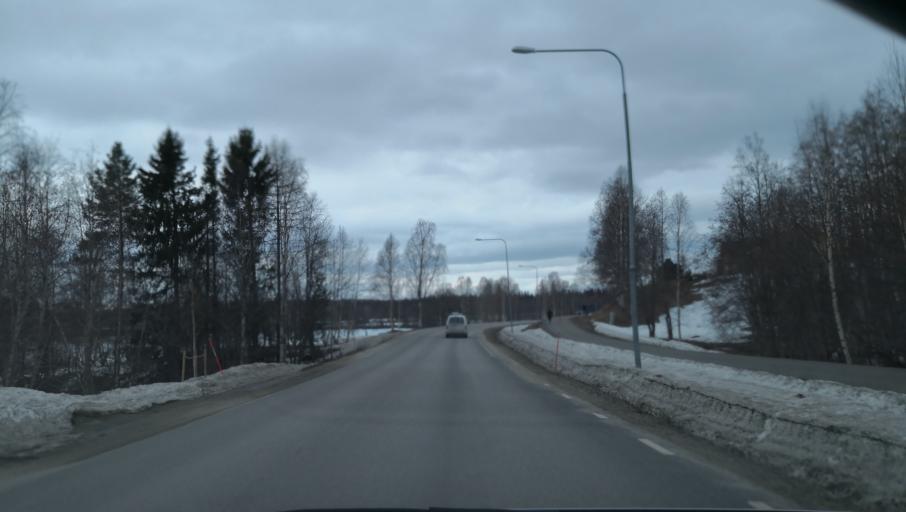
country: SE
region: Vaesterbotten
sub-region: Vannas Kommun
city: Vaennaes
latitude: 63.9175
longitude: 19.7912
